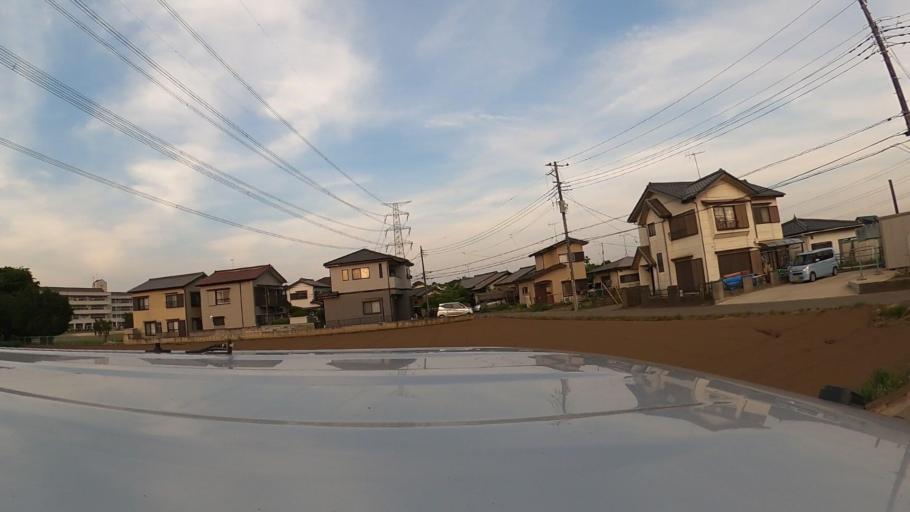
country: JP
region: Ibaraki
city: Ushiku
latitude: 36.0041
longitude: 140.1228
